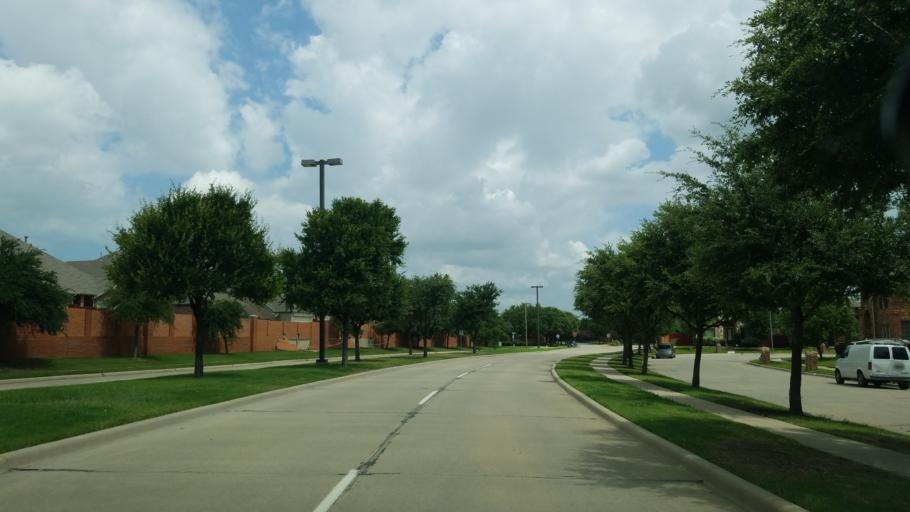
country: US
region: Texas
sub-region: Dallas County
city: Coppell
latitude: 32.9316
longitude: -96.9611
